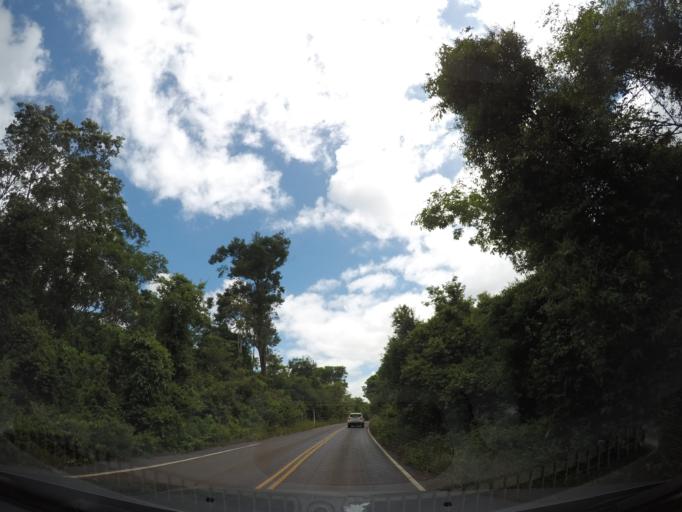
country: BR
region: Bahia
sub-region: Iraquara
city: Iraquara
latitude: -12.4814
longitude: -41.3628
